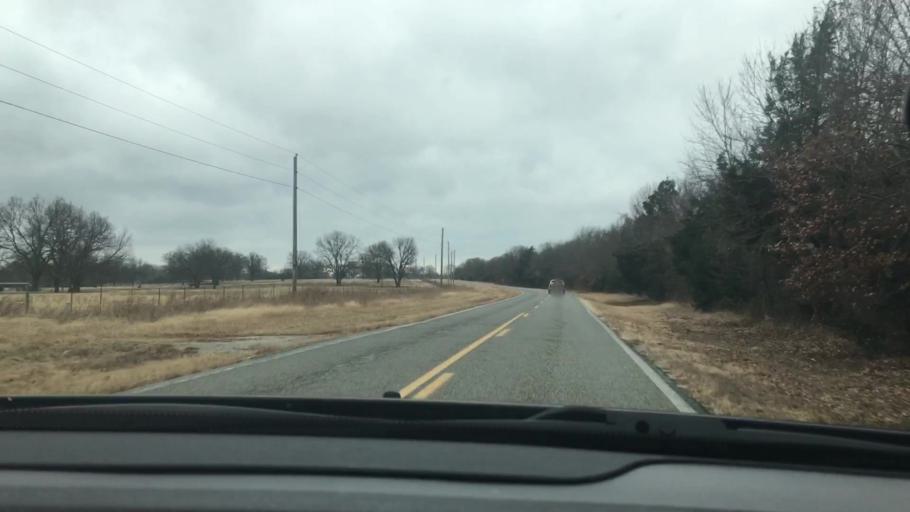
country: US
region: Oklahoma
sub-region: Johnston County
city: Tishomingo
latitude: 34.1916
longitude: -96.5788
